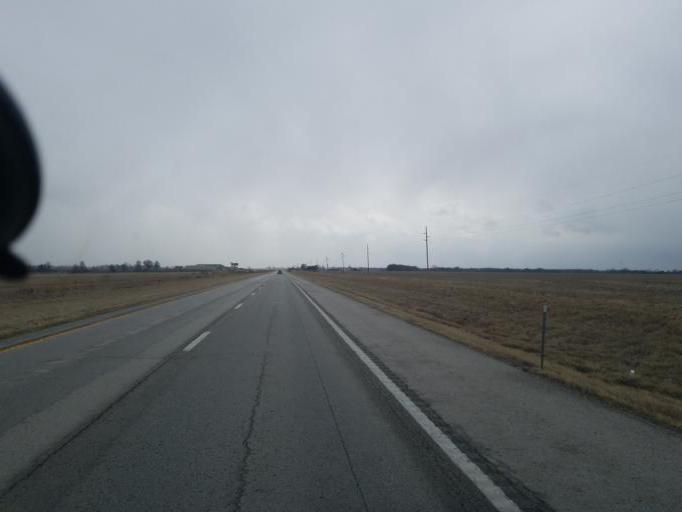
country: US
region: Missouri
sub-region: Randolph County
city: Moberly
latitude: 39.5515
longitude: -92.4551
